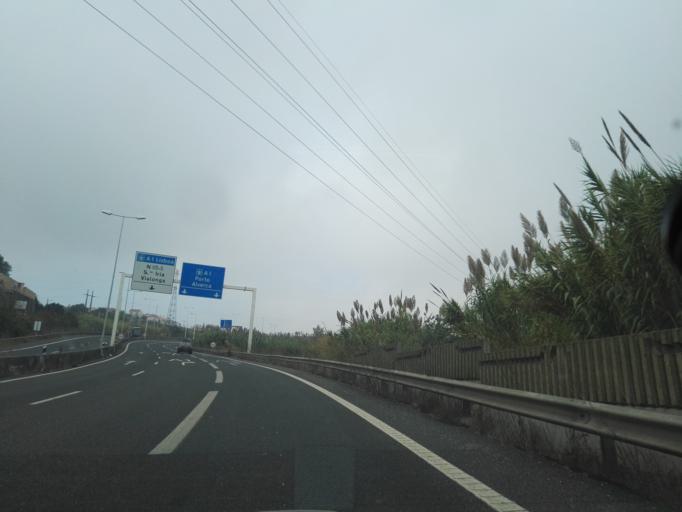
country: PT
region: Lisbon
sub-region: Loures
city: Santa Iria da Azoia
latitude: 38.8479
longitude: -9.0842
